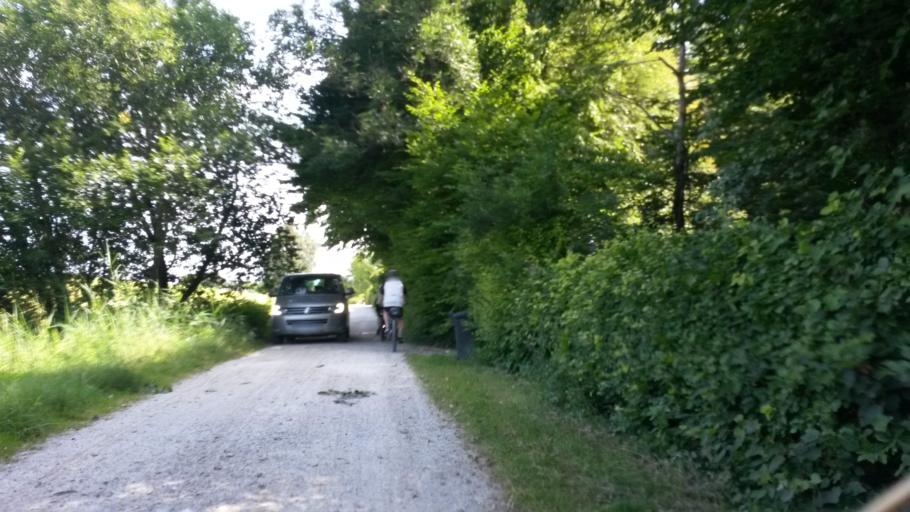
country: DE
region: Bavaria
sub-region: Upper Bavaria
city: Gstadt am Chiemsee
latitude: 47.8816
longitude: 12.3900
